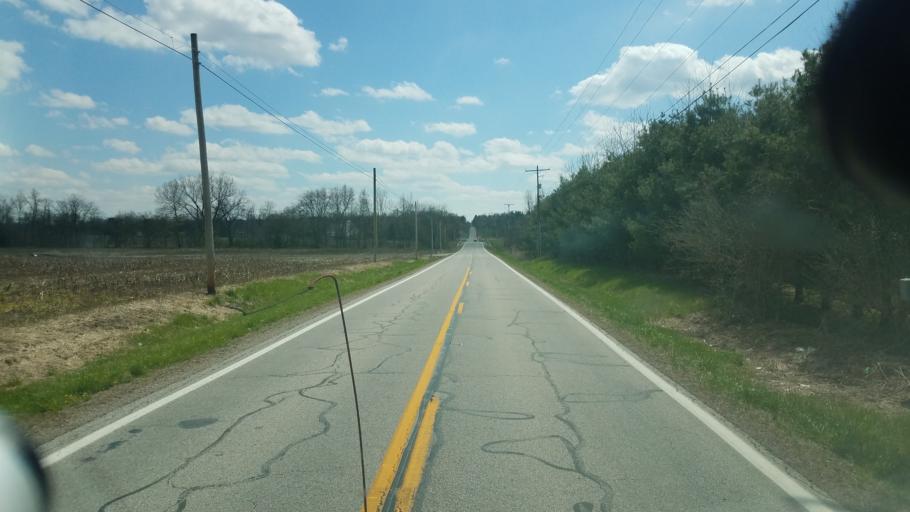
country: US
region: Ohio
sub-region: Licking County
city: Johnstown
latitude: 40.1187
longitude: -82.6604
